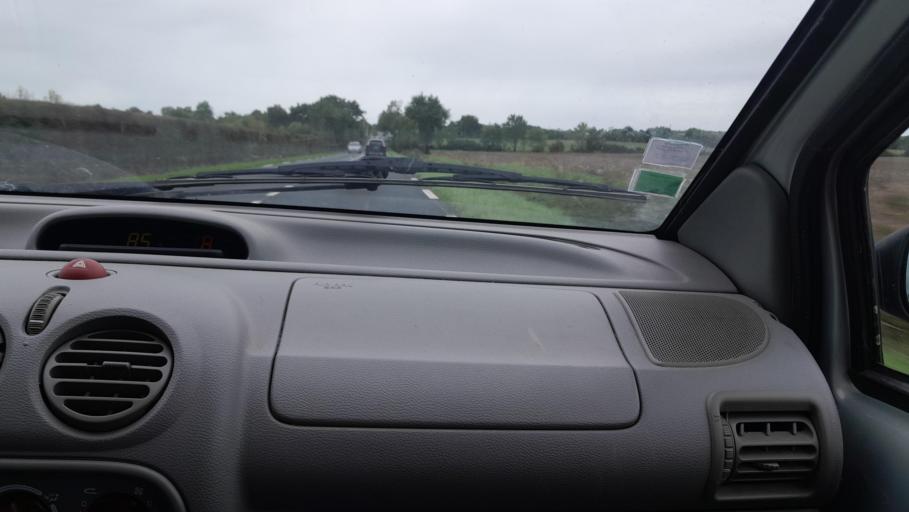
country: FR
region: Pays de la Loire
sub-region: Departement de la Loire-Atlantique
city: Saint-Mars-la-Jaille
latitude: 47.4840
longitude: -1.1736
